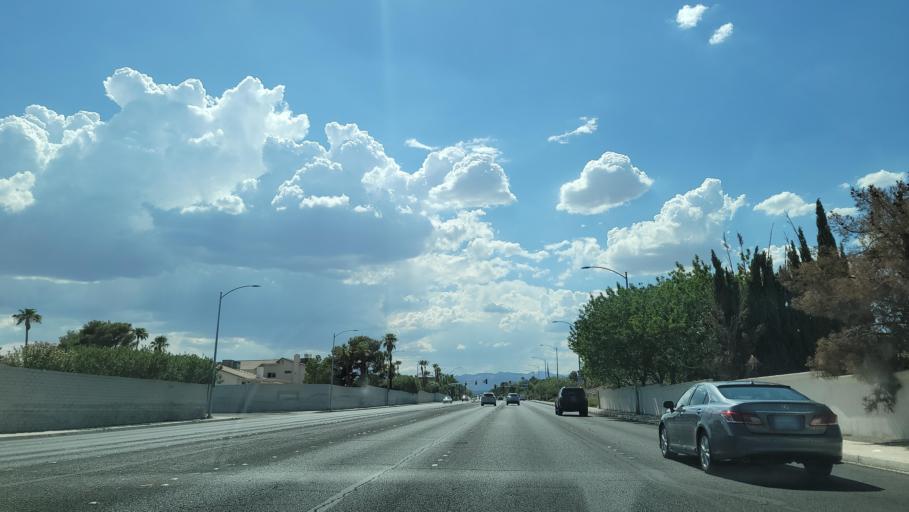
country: US
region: Nevada
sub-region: Clark County
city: Spring Valley
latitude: 36.1295
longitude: -115.2399
